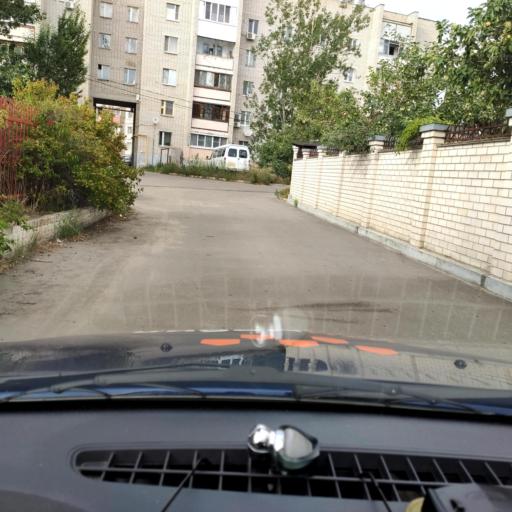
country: RU
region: Voronezj
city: Podgornoye
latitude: 51.7251
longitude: 39.1902
